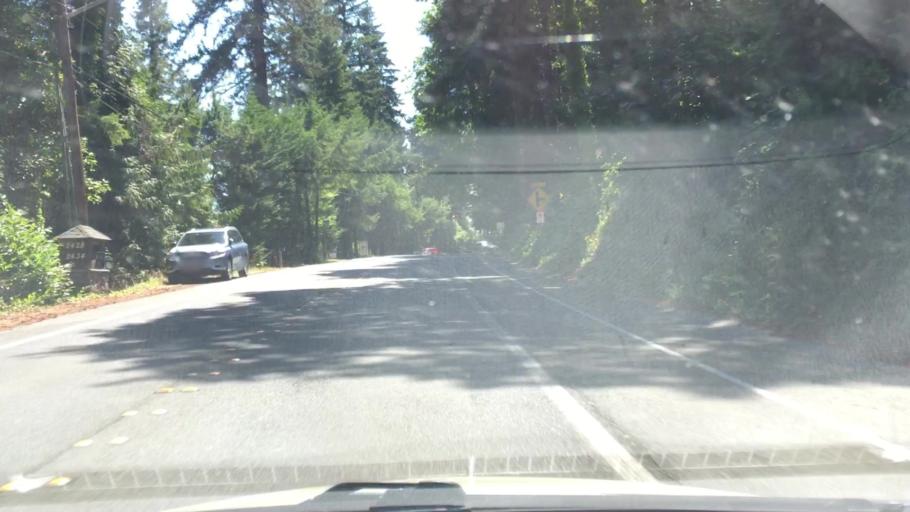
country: US
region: Washington
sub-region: King County
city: Sammamish
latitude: 47.6321
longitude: -122.0892
